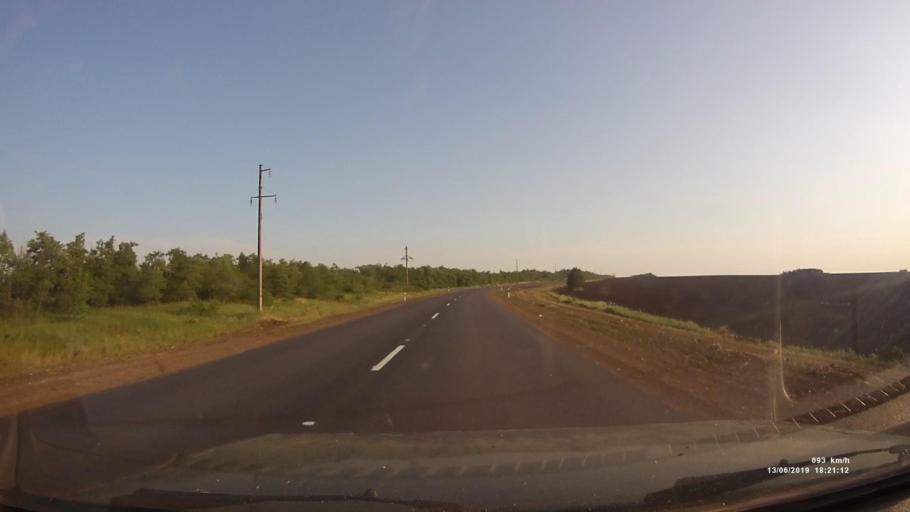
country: RU
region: Rostov
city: Kazanskaya
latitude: 49.8736
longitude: 41.2939
